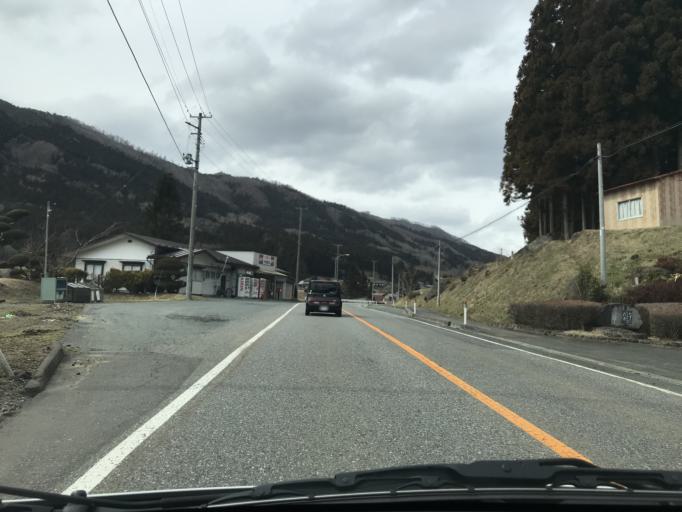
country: JP
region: Iwate
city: Tono
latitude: 39.3349
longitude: 141.4478
